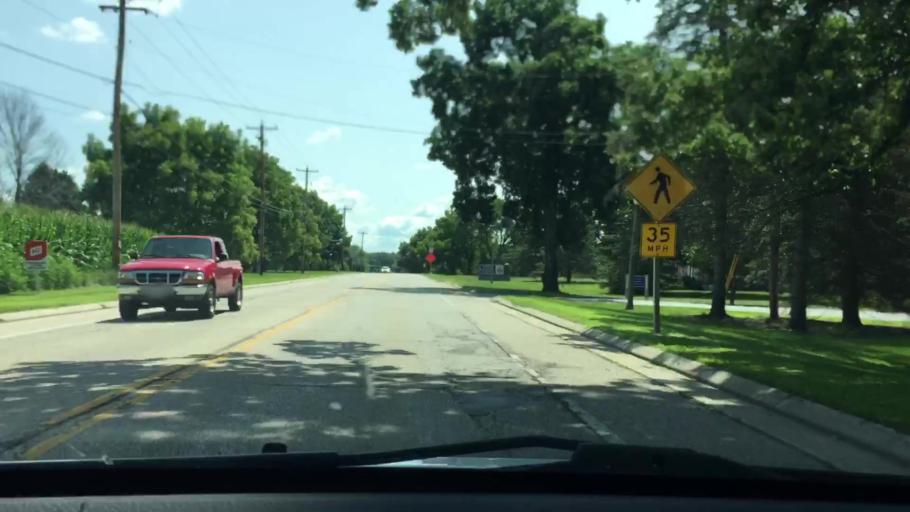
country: US
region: Wisconsin
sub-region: Waukesha County
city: Dousman
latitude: 43.0237
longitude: -88.4693
